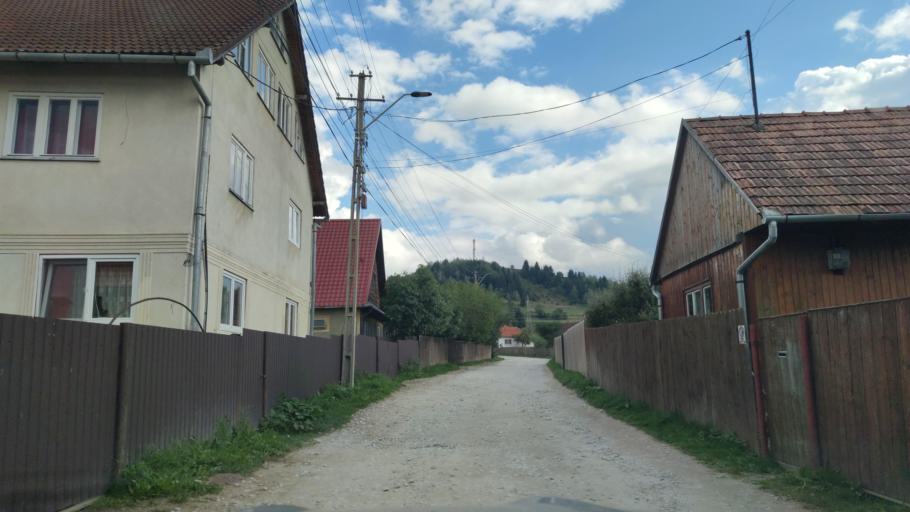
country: RO
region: Harghita
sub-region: Municipiul Gheorgheni
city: Gheorgheni
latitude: 46.7254
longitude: 25.6349
